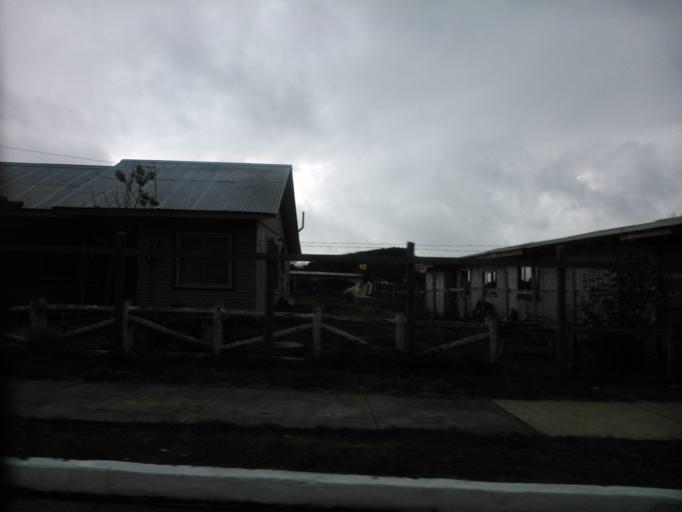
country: CL
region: Araucania
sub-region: Provincia de Cautin
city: Carahue
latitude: -38.8113
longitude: -73.3988
